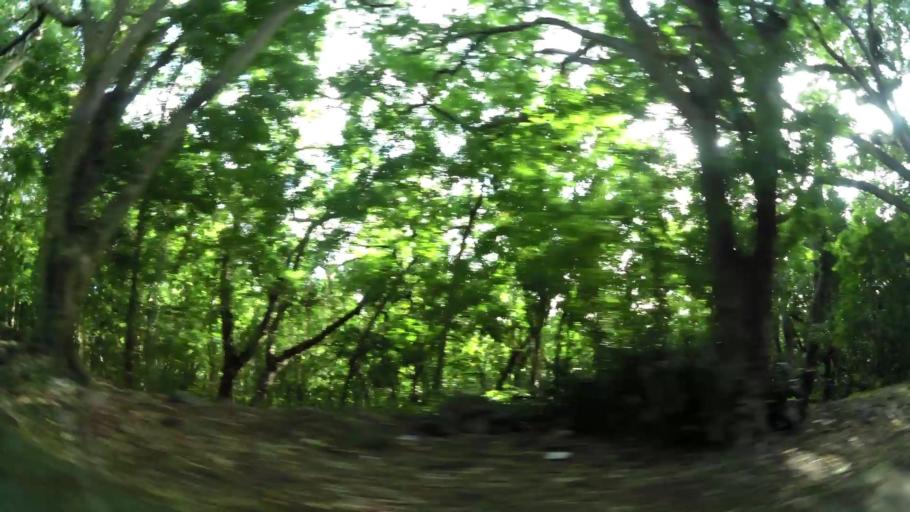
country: GP
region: Guadeloupe
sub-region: Guadeloupe
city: Pointe-Noire
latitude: 16.1865
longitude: -61.7735
